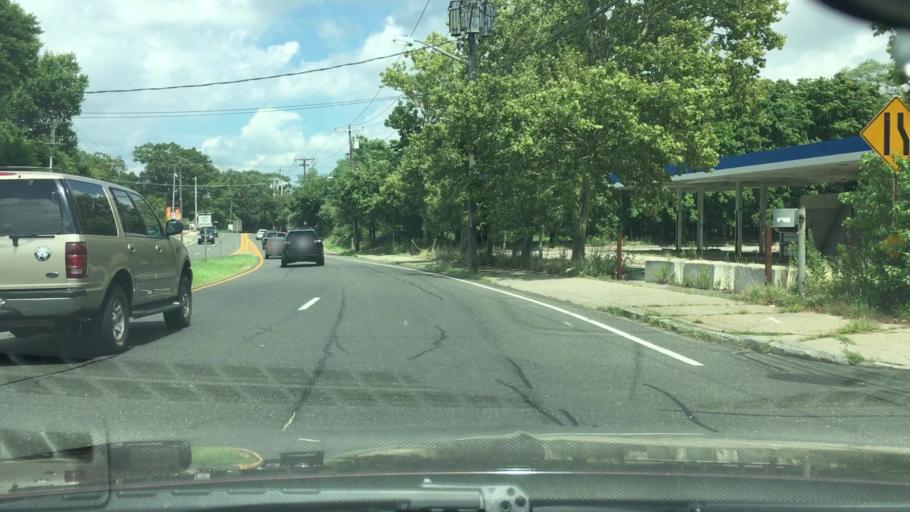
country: US
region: New York
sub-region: Suffolk County
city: Hauppauge
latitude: 40.8102
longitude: -73.2170
